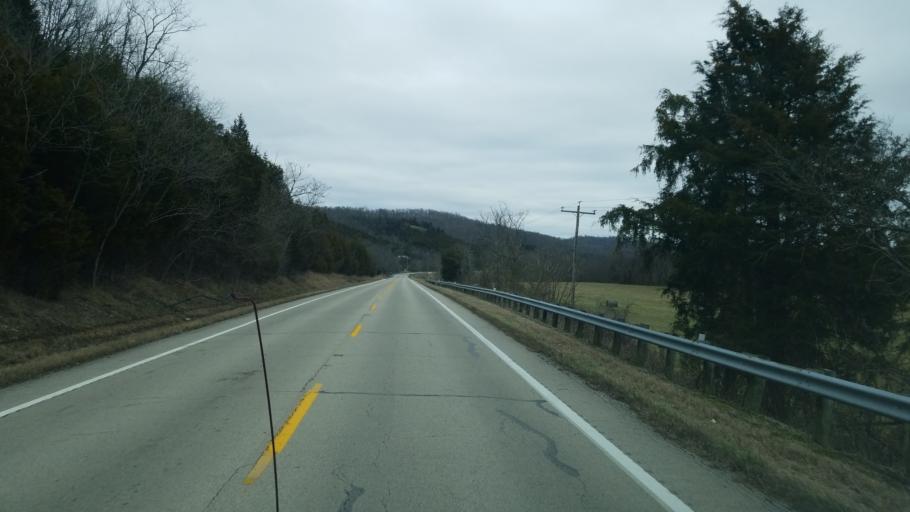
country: US
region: Ohio
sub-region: Adams County
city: Manchester
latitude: 38.7063
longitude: -83.5257
